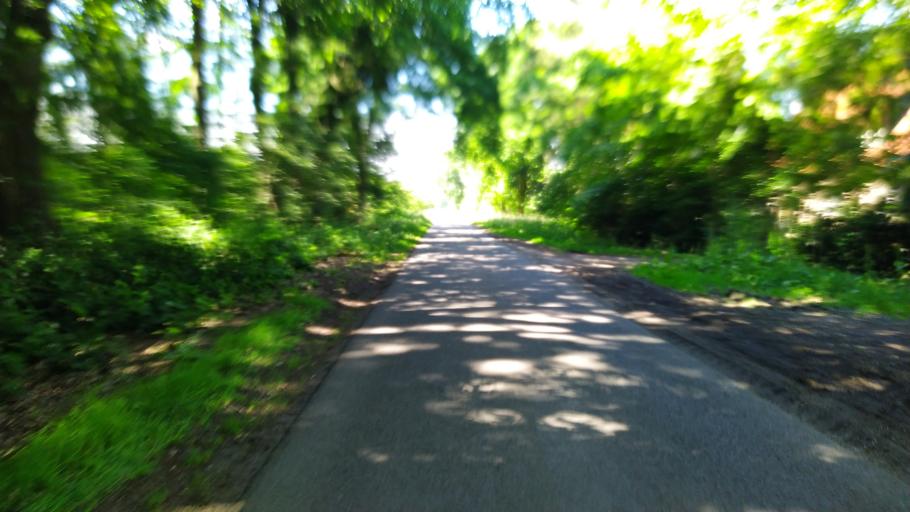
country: DE
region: Lower Saxony
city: Oldendorf
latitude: 53.5595
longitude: 9.2291
